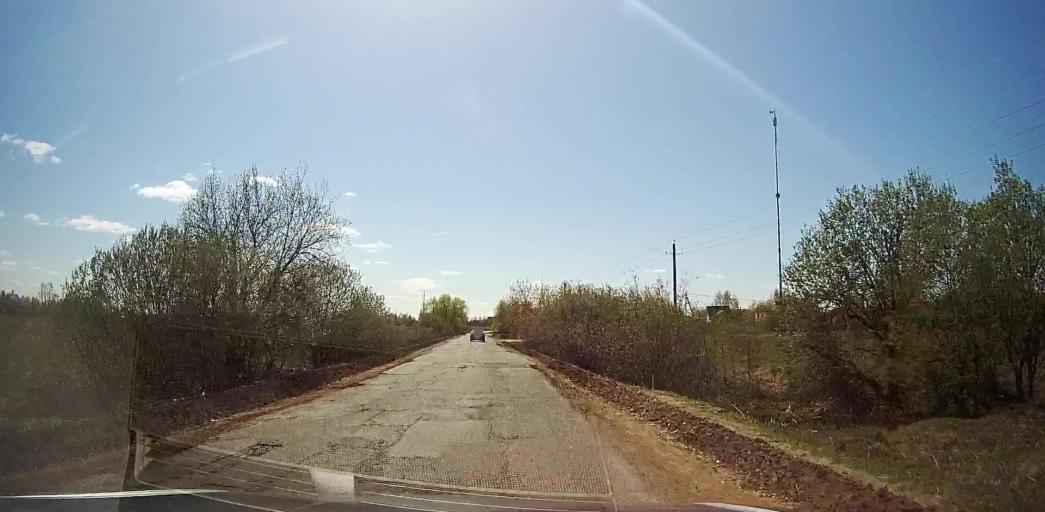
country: RU
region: Moskovskaya
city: Malyshevo
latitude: 55.4614
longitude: 38.3805
